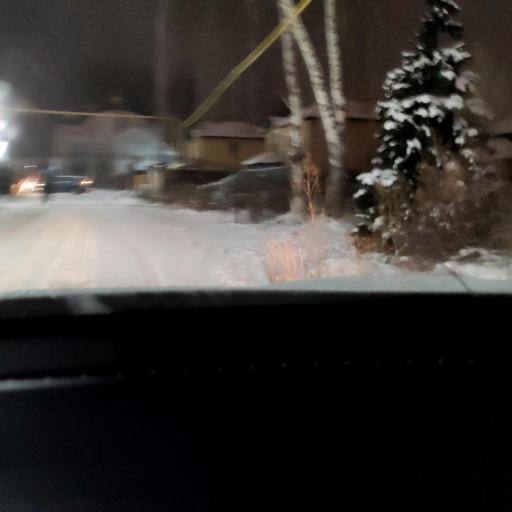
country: RU
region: Tatarstan
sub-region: Gorod Kazan'
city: Kazan
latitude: 55.8442
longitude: 49.1577
